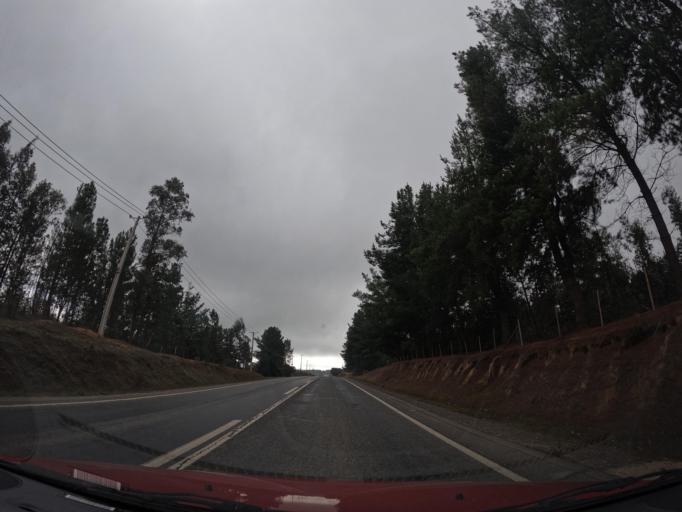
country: CL
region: Maule
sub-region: Provincia de Cauquenes
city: Cauquenes
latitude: -36.2487
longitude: -72.5483
